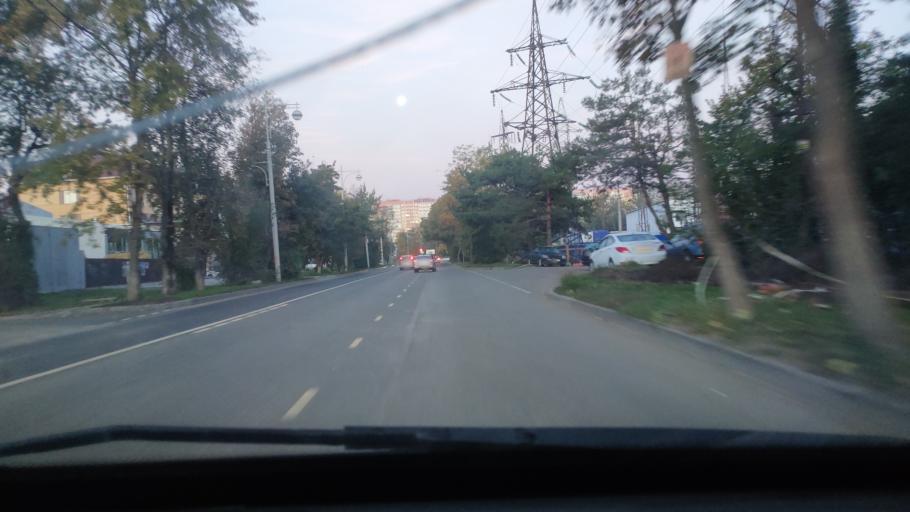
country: RU
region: Krasnodarskiy
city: Krasnodar
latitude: 45.0724
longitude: 38.9901
